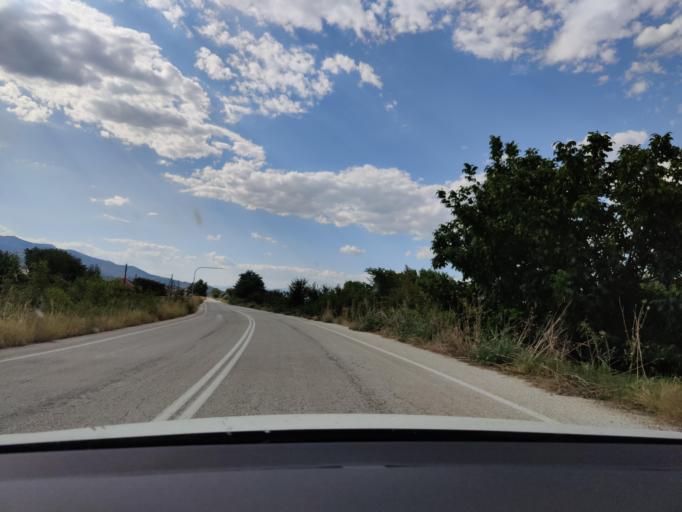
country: GR
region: Central Macedonia
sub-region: Nomos Serron
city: Strymoniko
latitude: 41.0880
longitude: 23.2841
